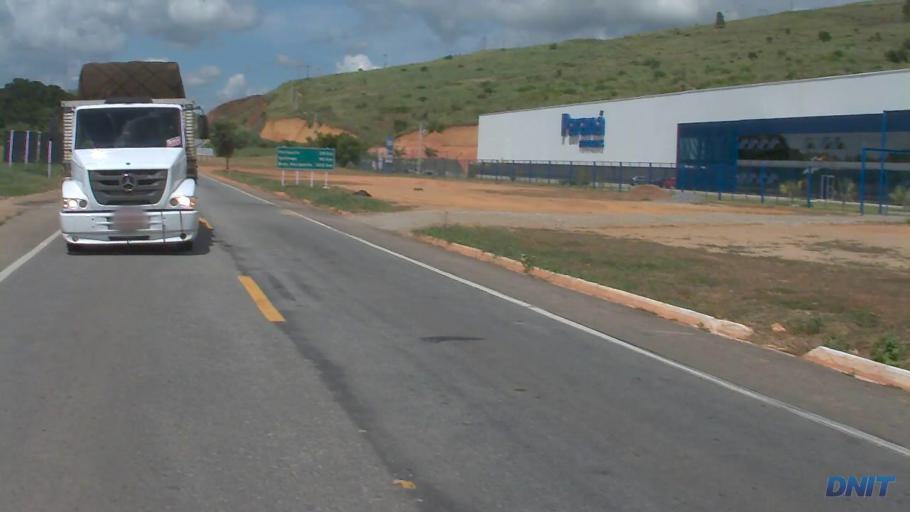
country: BR
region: Minas Gerais
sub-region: Governador Valadares
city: Governador Valadares
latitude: -18.9253
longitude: -42.0360
